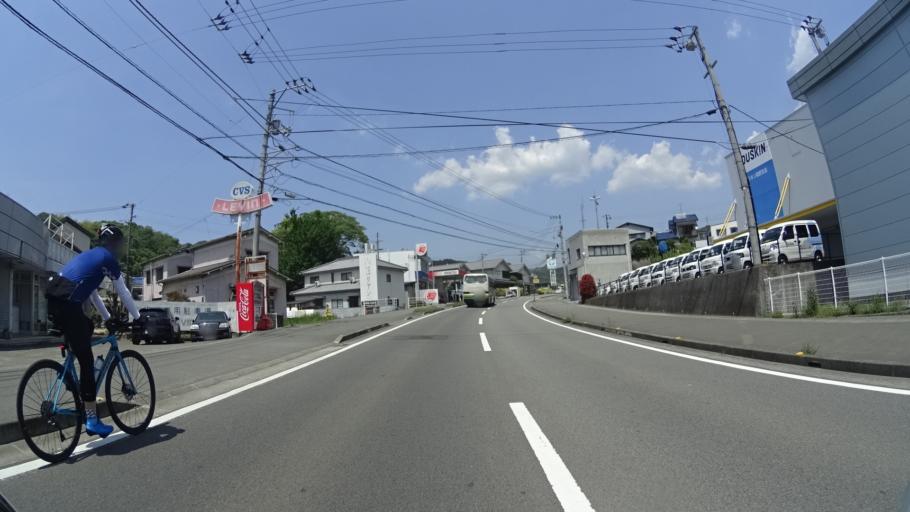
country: JP
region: Ehime
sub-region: Shikoku-chuo Shi
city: Matsuyama
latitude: 33.8551
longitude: 132.8102
